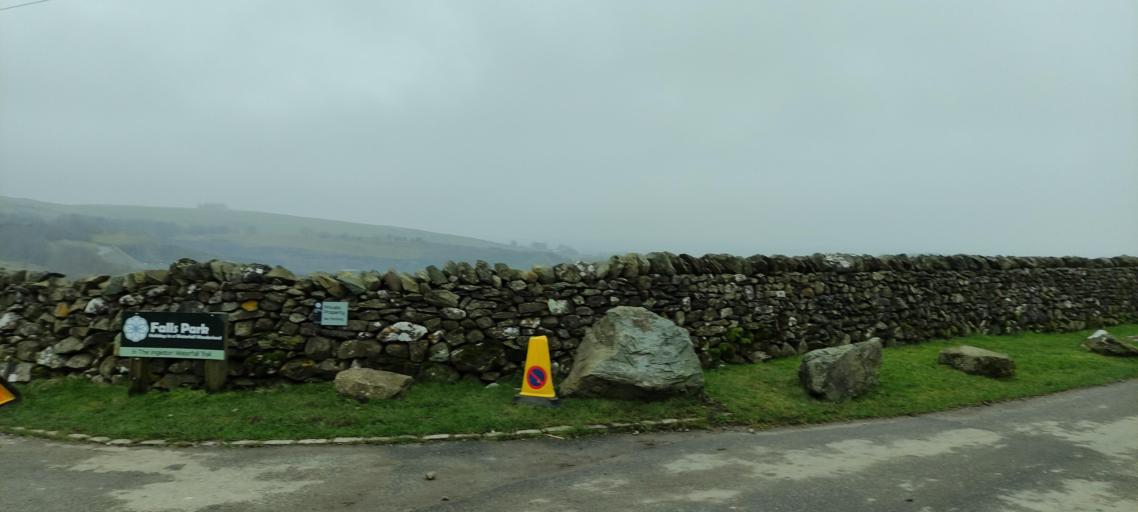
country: GB
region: England
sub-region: North Yorkshire
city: Ingleton
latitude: 54.1694
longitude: -2.4536
